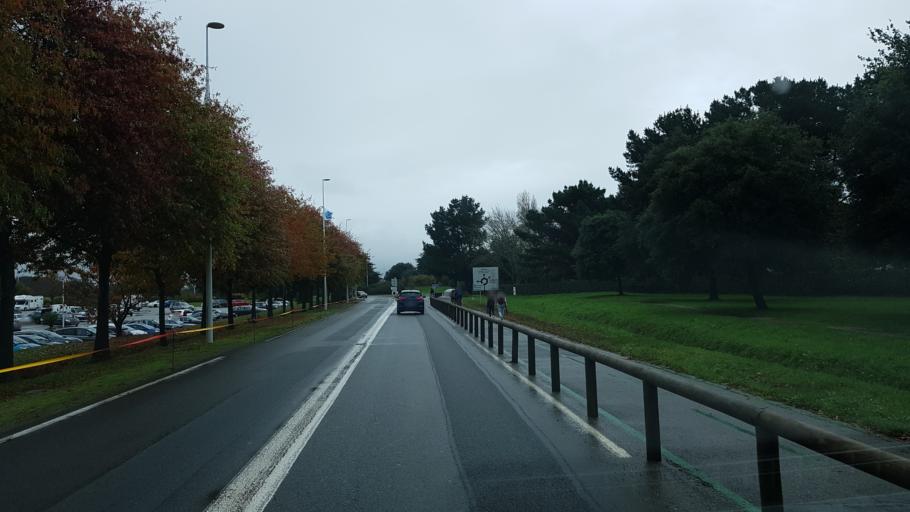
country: FR
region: Brittany
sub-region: Departement du Morbihan
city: Arzon
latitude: 47.5423
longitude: -2.8814
